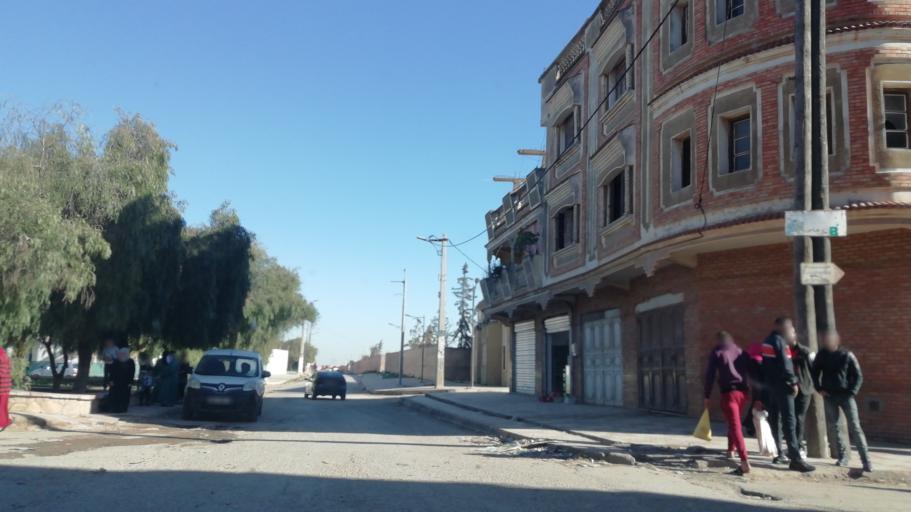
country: DZ
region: Oran
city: Bir el Djir
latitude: 35.7248
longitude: -0.5358
